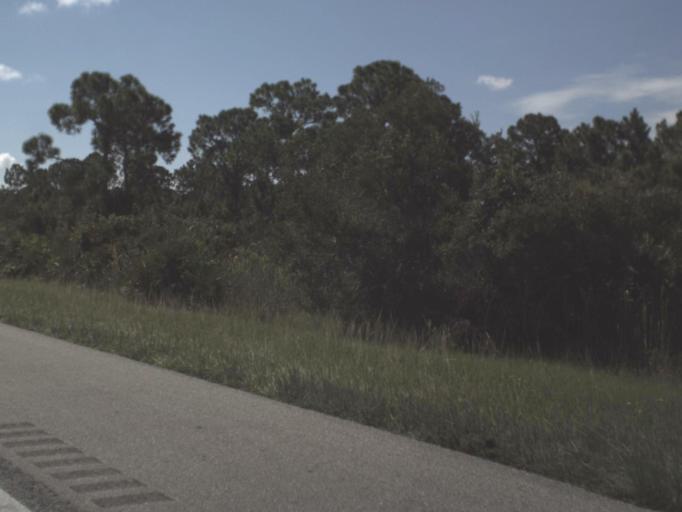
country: US
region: Florida
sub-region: Lee County
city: Burnt Store Marina
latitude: 26.8307
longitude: -81.9551
